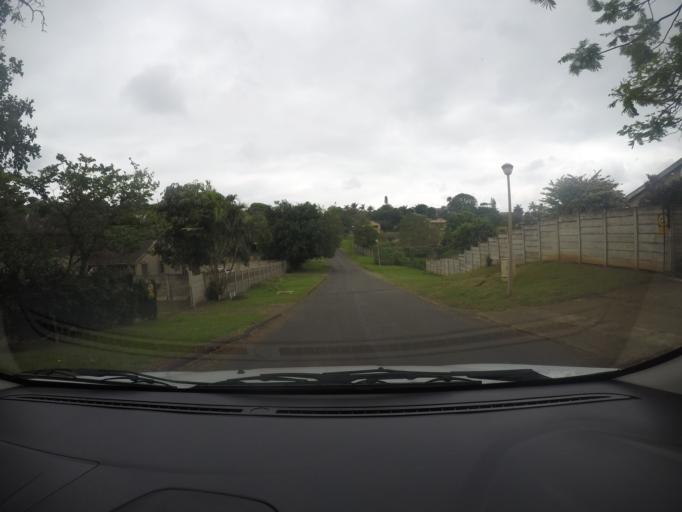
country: ZA
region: KwaZulu-Natal
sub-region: uThungulu District Municipality
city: Empangeni
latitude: -28.7580
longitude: 31.8852
